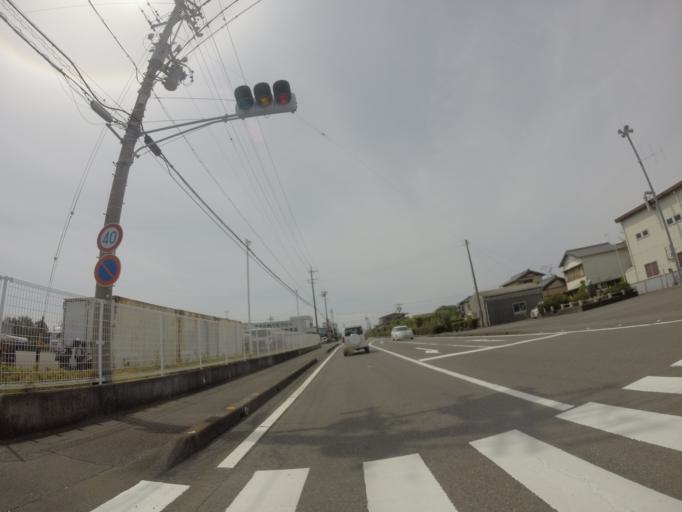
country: JP
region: Shizuoka
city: Yaizu
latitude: 34.7821
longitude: 138.2986
